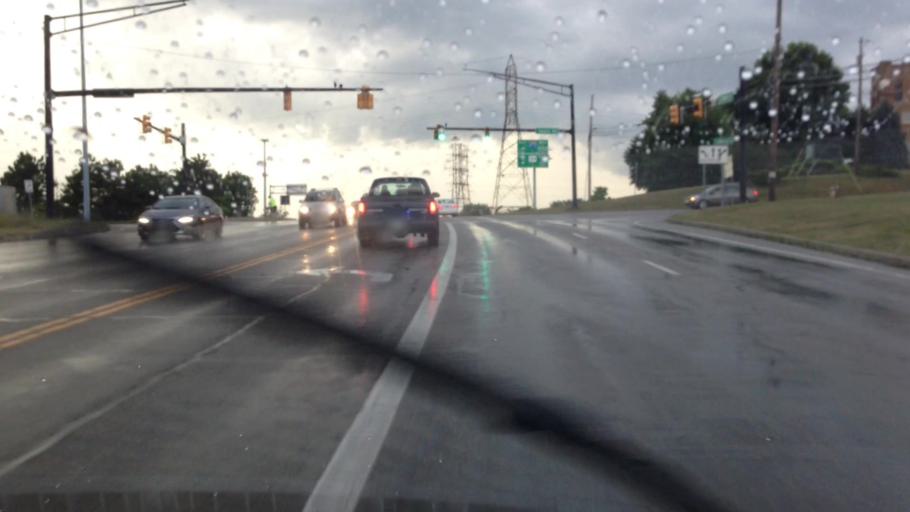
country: US
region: Ohio
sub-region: Summit County
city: Portage Lakes
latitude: 41.0229
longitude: -81.5263
